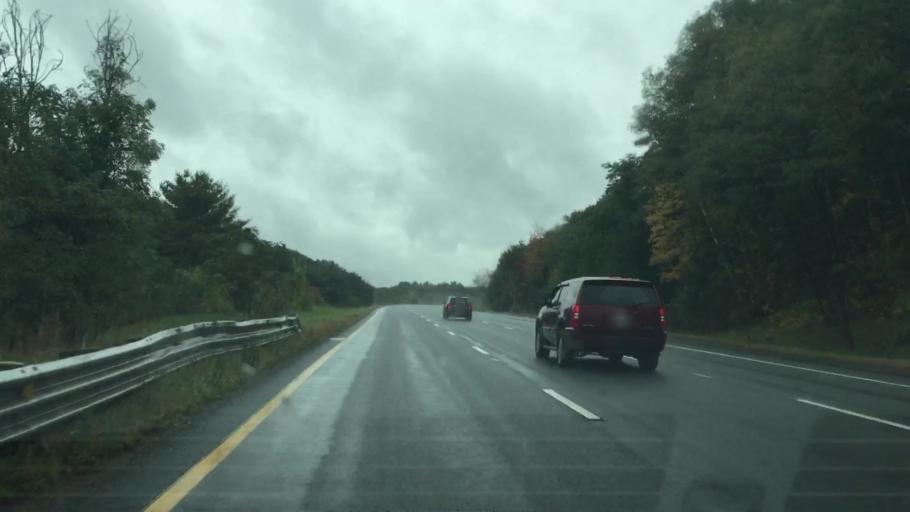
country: US
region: Massachusetts
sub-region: Essex County
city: Merrimac
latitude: 42.8062
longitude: -71.0337
